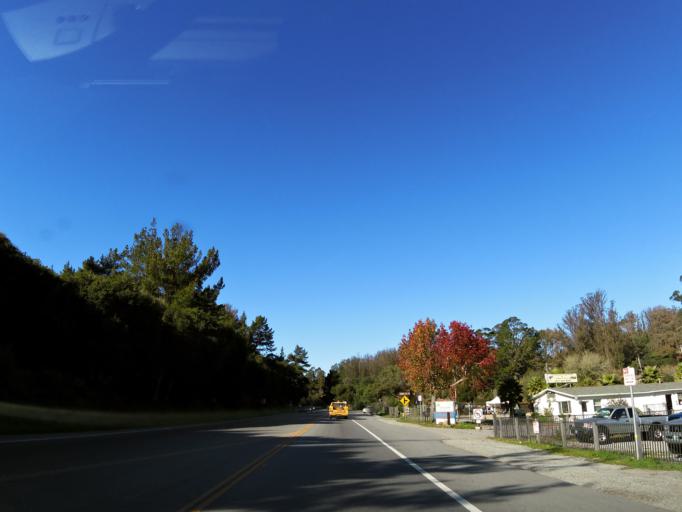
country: US
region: California
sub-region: Monterey County
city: Prunedale
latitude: 36.8035
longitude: -121.6673
